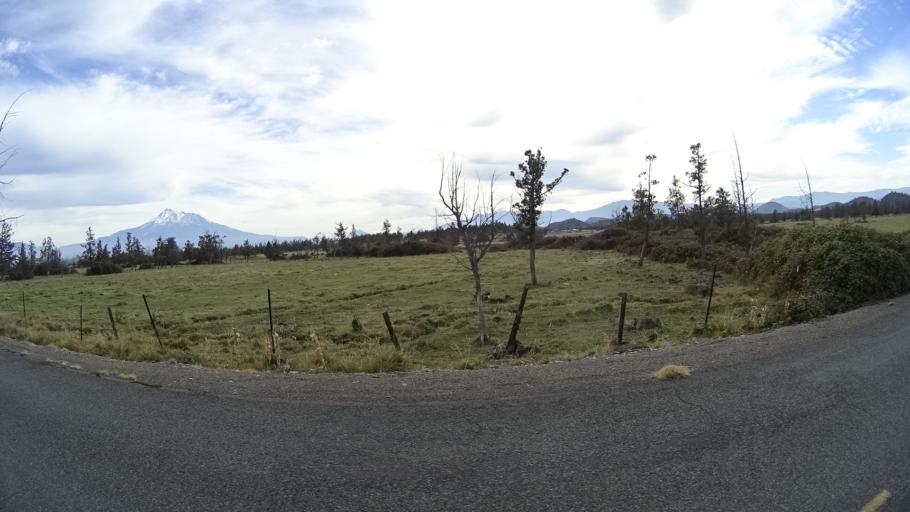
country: US
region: California
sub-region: Siskiyou County
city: Montague
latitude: 41.6385
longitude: -122.4293
